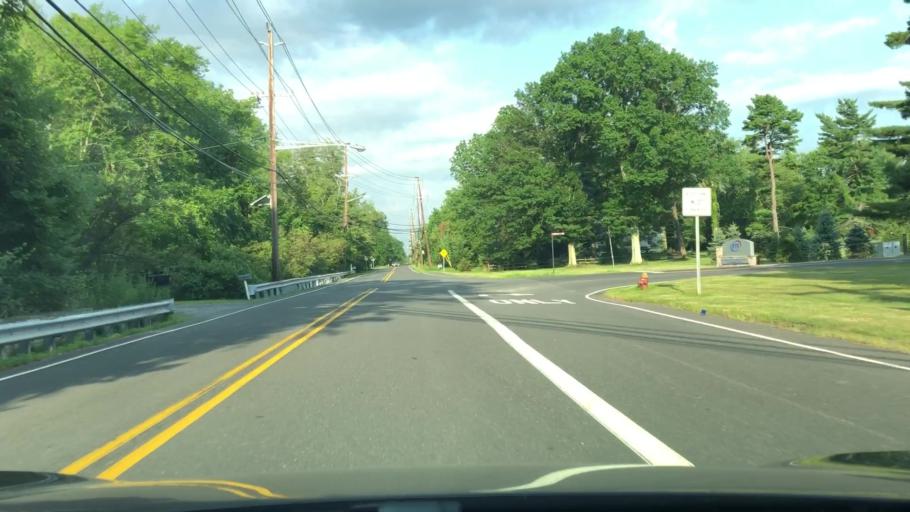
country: US
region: New Jersey
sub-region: Mercer County
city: Lawrenceville
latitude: 40.3412
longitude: -74.7104
